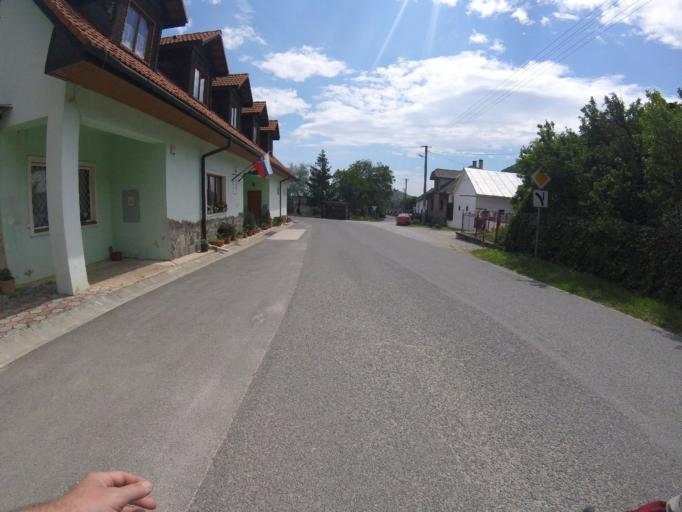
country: SK
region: Kosicky
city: Medzev
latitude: 48.6287
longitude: 20.8539
